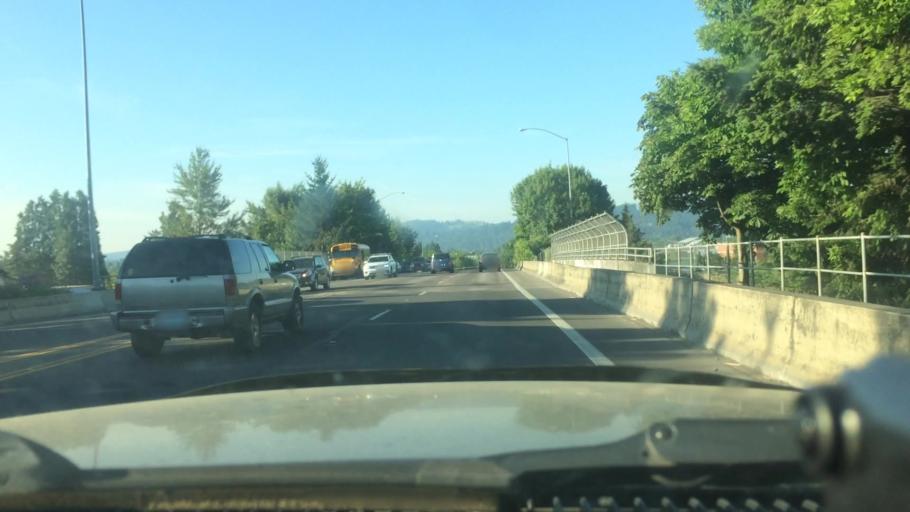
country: US
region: Oregon
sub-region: Lane County
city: Eugene
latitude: 44.0607
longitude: -123.1175
